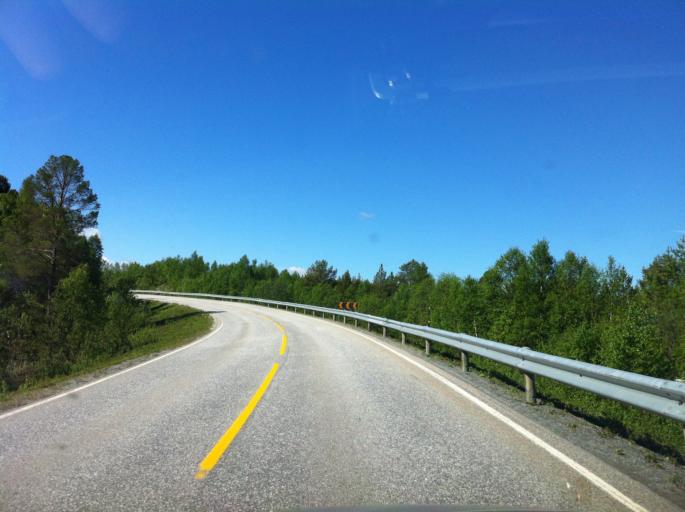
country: NO
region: Sor-Trondelag
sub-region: Roros
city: Roros
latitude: 62.6132
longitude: 11.8471
